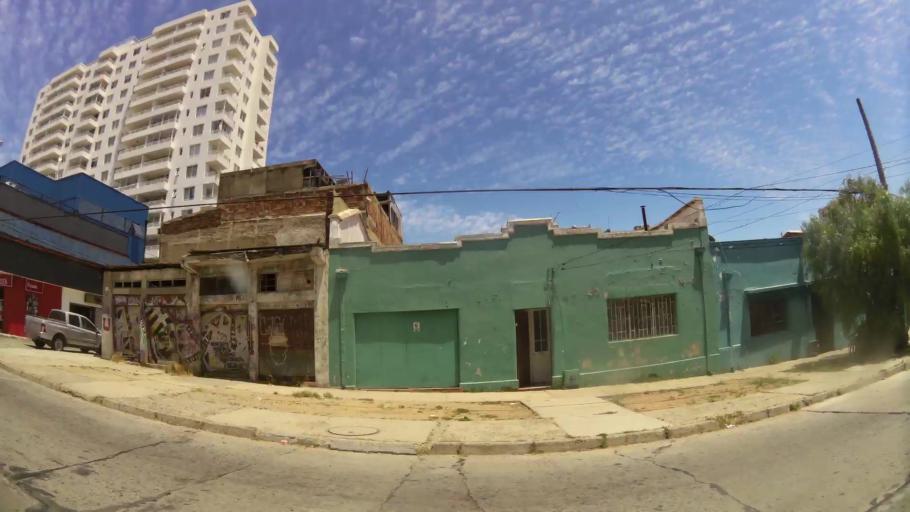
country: CL
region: Valparaiso
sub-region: Provincia de Valparaiso
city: Valparaiso
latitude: -33.0418
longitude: -71.5899
